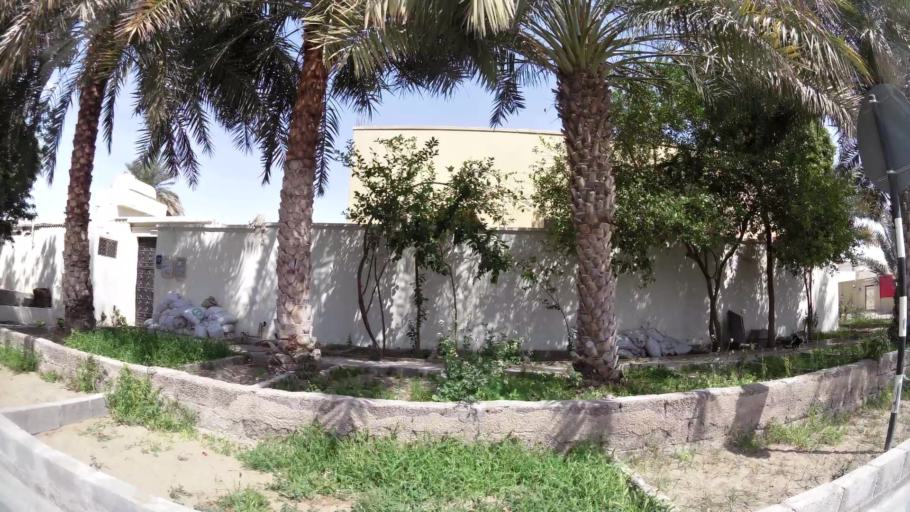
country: AE
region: Abu Dhabi
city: Abu Dhabi
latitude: 24.2892
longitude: 54.6524
